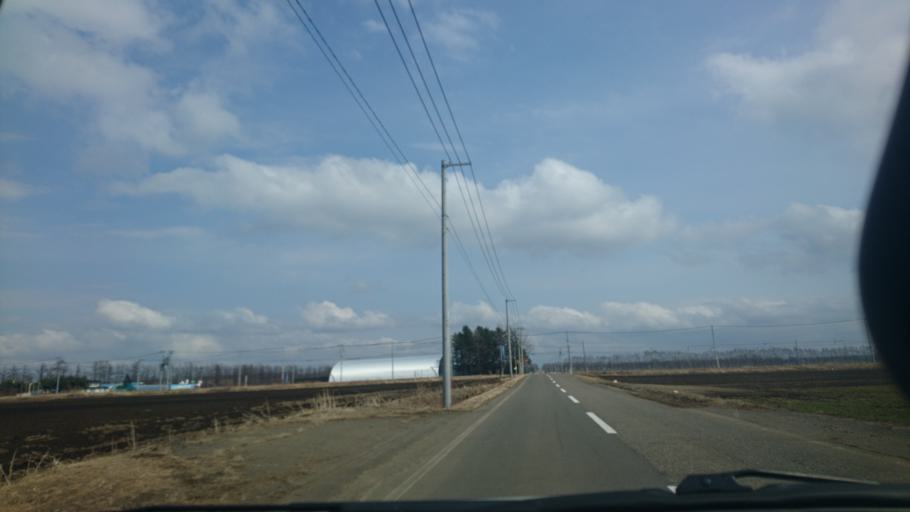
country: JP
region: Hokkaido
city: Otofuke
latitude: 43.2071
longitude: 143.2734
